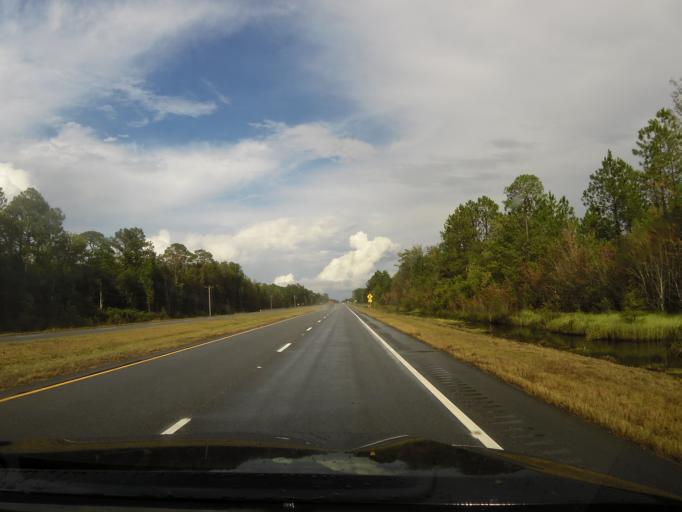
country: US
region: Georgia
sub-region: Liberty County
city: Walthourville
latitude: 31.7601
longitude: -81.6579
